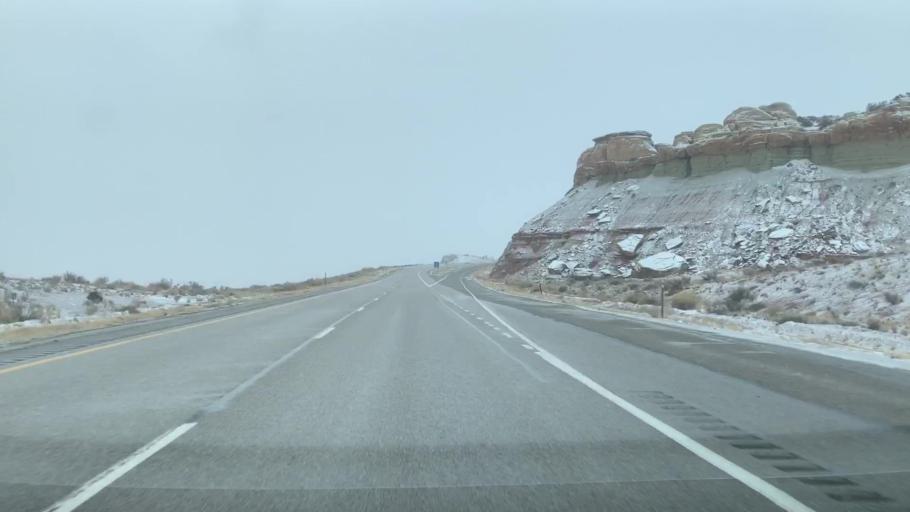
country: US
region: Utah
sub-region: Emery County
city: Ferron
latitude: 38.8370
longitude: -111.1043
